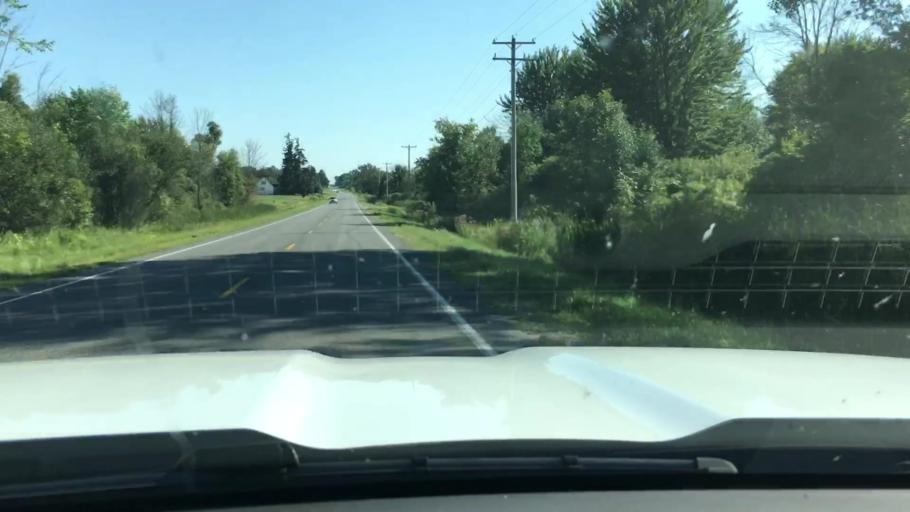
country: US
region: Michigan
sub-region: Muskegon County
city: Ravenna
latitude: 43.1744
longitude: -85.9278
